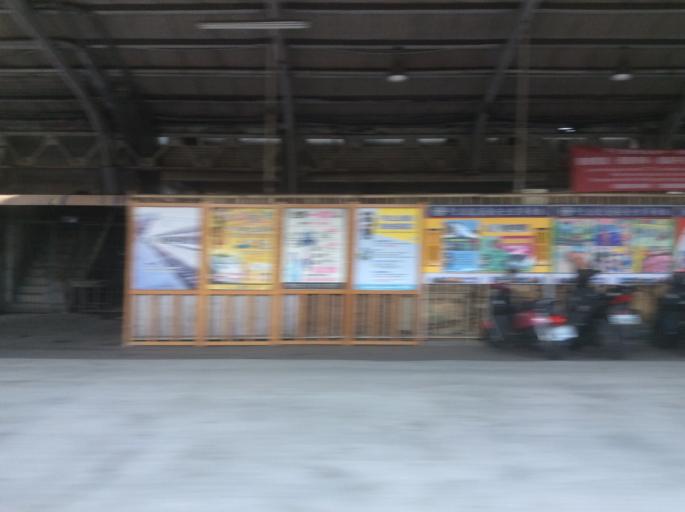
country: TW
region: Taiwan
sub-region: Tainan
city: Tainan
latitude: 22.9975
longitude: 120.2129
